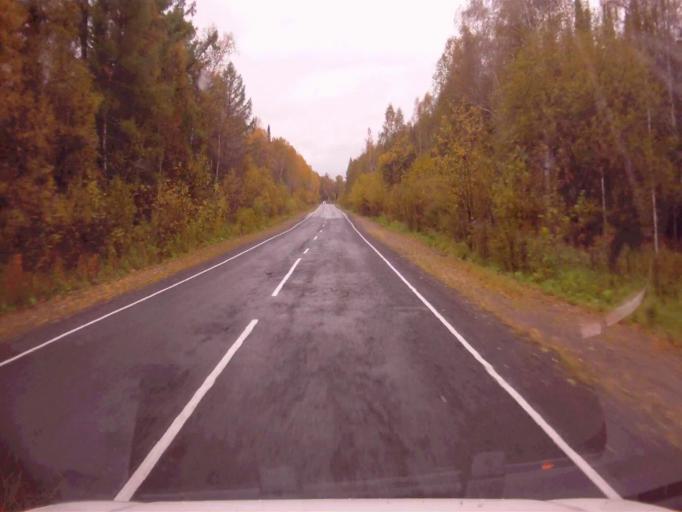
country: RU
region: Chelyabinsk
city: Nizhniy Ufaley
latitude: 56.0642
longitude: 59.9997
